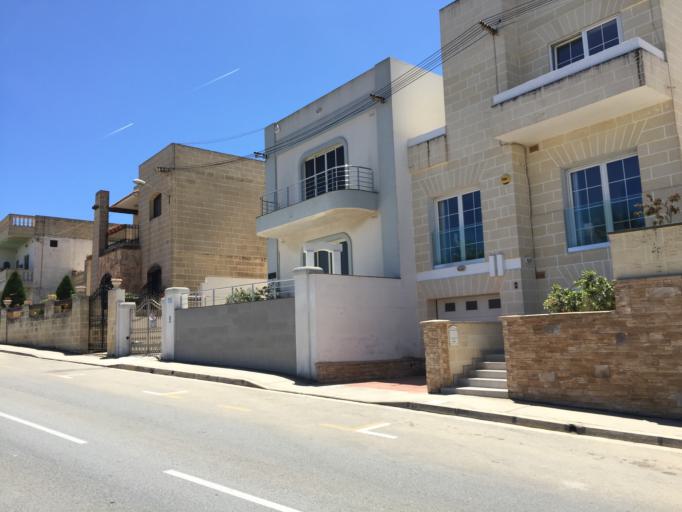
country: MT
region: Is-Swieqi
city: Swieqi
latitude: 35.9285
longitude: 14.4844
